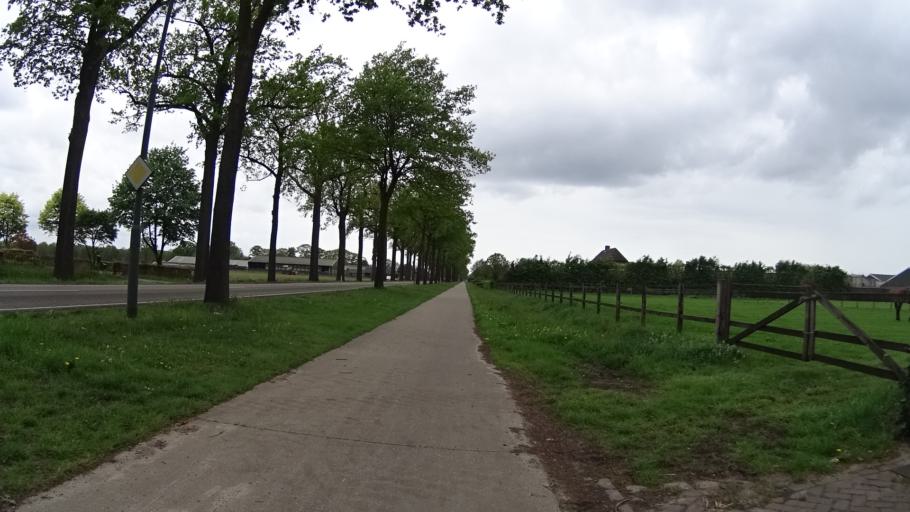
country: NL
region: North Brabant
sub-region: Gemeente Veghel
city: Erp
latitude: 51.6029
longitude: 5.5943
